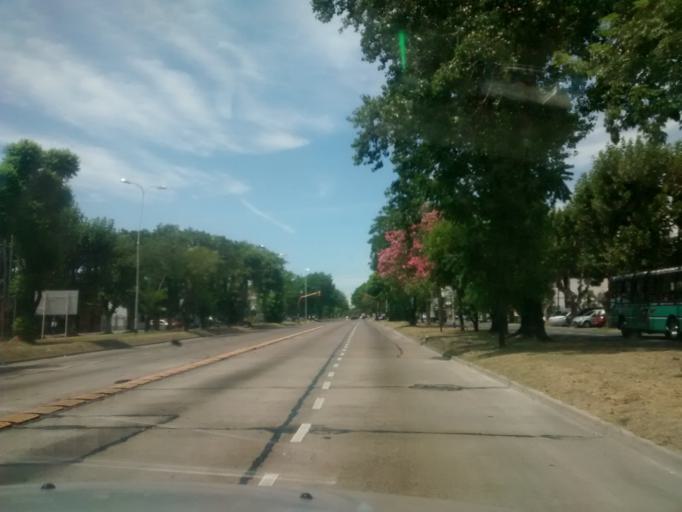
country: AR
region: Buenos Aires
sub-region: Partido de Avellaneda
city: Avellaneda
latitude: -34.6864
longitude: -58.3405
